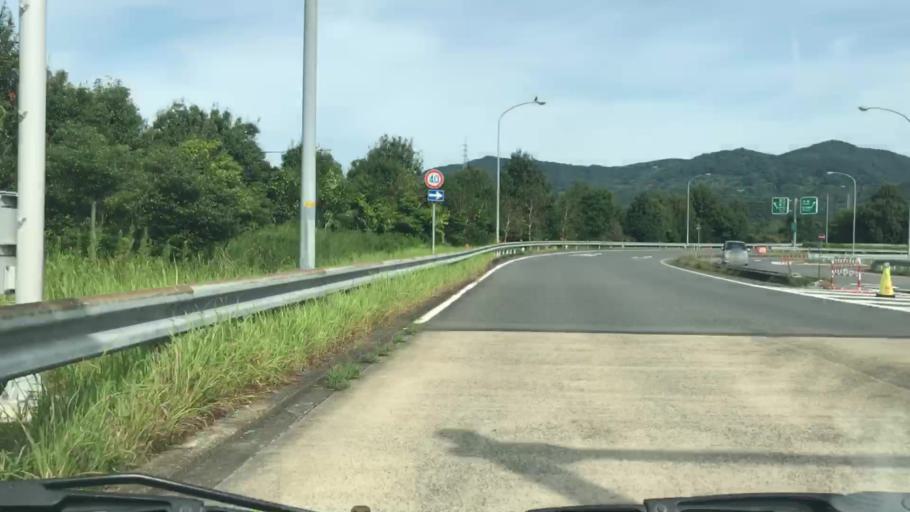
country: JP
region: Saga Prefecture
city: Takeocho-takeo
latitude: 33.2171
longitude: 130.0489
